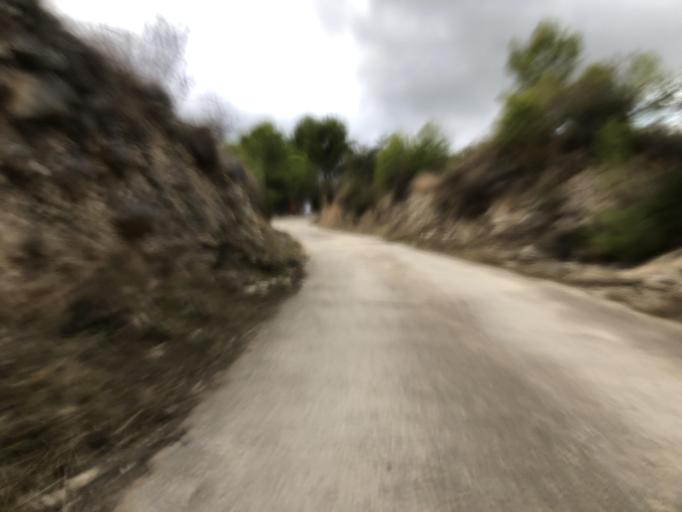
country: ES
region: Valencia
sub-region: Provincia de Alicante
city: Polop
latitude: 38.6358
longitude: -0.1491
